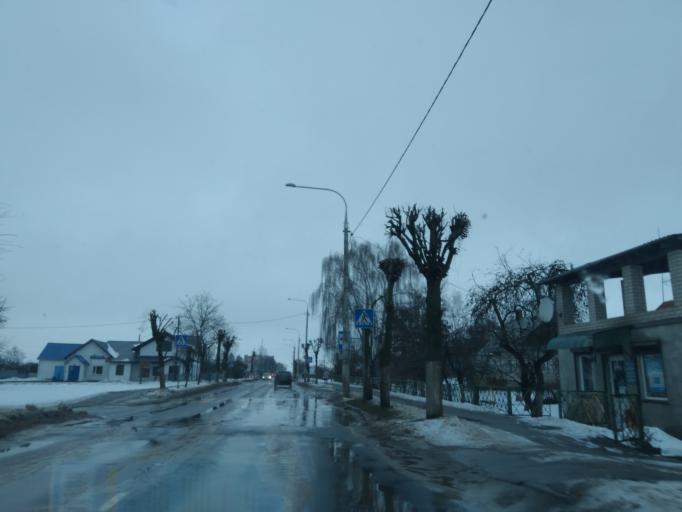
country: BY
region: Minsk
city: Nyasvizh
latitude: 53.2255
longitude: 26.6698
